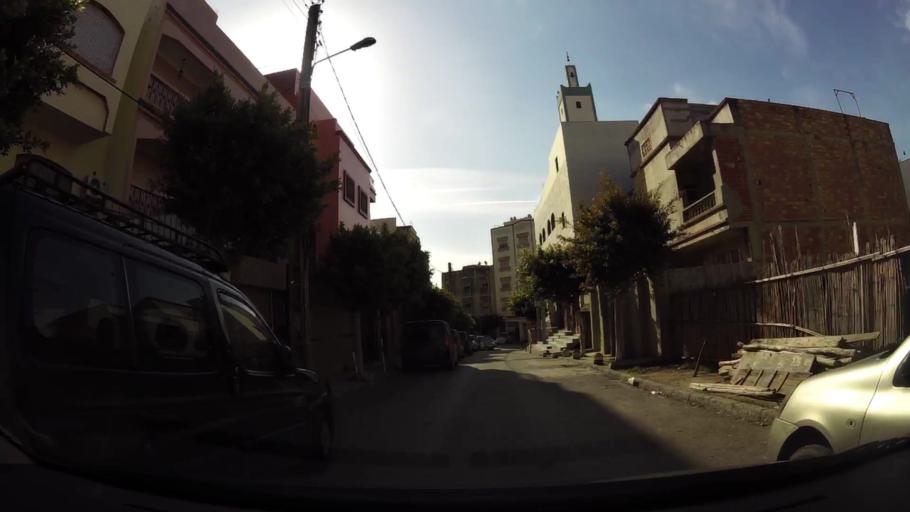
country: MA
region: Tanger-Tetouan
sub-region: Tanger-Assilah
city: Tangier
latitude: 35.7626
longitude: -5.7919
